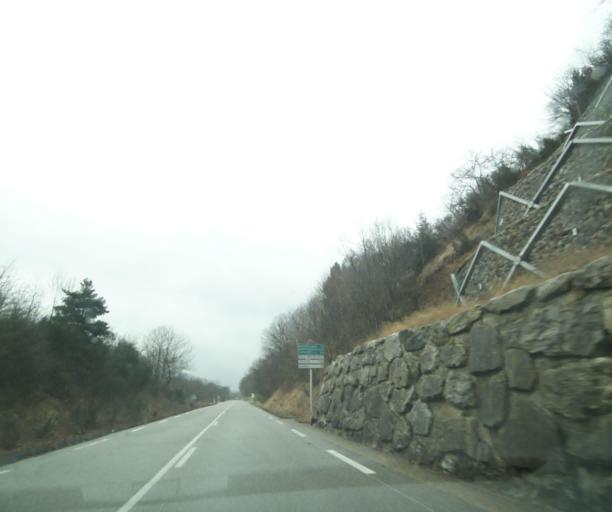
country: FR
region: Rhone-Alpes
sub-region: Departement de l'Ardeche
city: Thueyts
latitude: 44.6643
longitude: 4.1245
